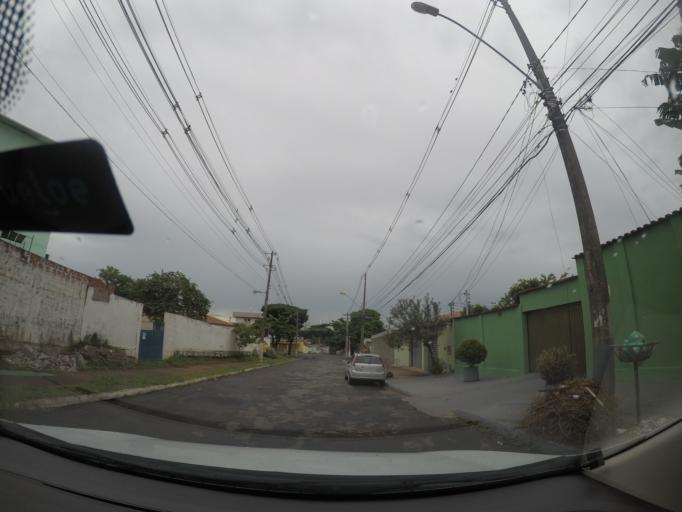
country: BR
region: Goias
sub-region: Goiania
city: Goiania
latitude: -16.6853
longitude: -49.2384
